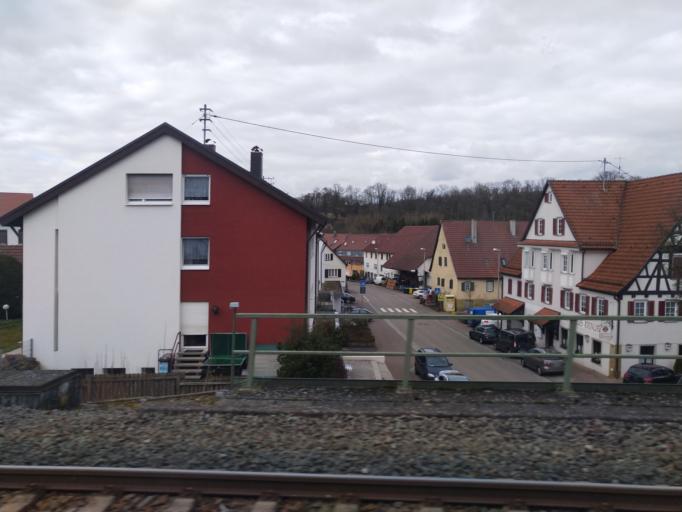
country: DE
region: Baden-Wuerttemberg
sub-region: Regierungsbezirk Stuttgart
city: Burgstetten
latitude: 48.9292
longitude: 9.3709
